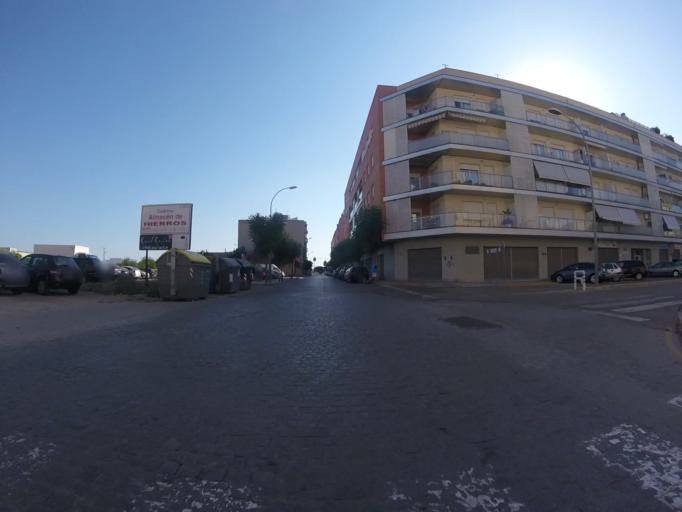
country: ES
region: Valencia
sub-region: Provincia de Castello
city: Benicarlo
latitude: 40.4219
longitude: 0.4282
